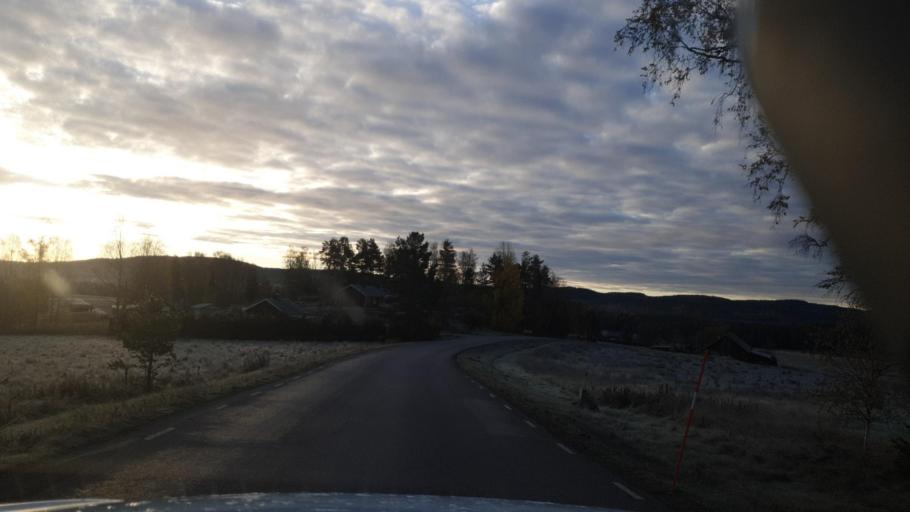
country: SE
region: Vaermland
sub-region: Eda Kommun
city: Charlottenberg
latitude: 59.7446
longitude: 12.1654
